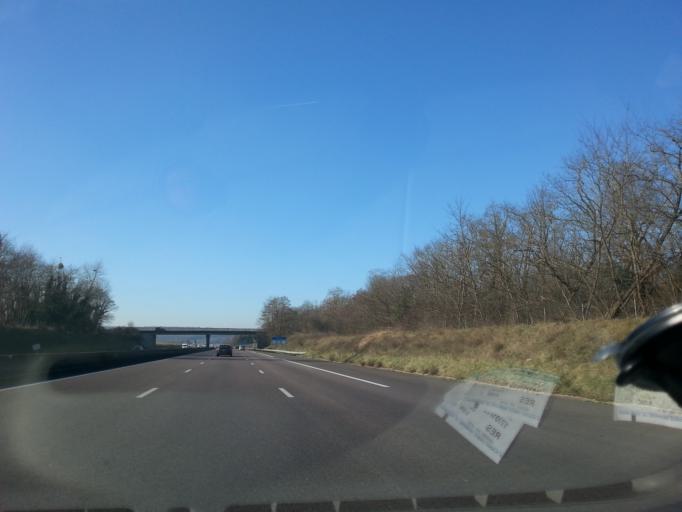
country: FR
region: Ile-de-France
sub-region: Departement des Yvelines
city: Buchelay
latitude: 48.9888
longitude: 1.6559
